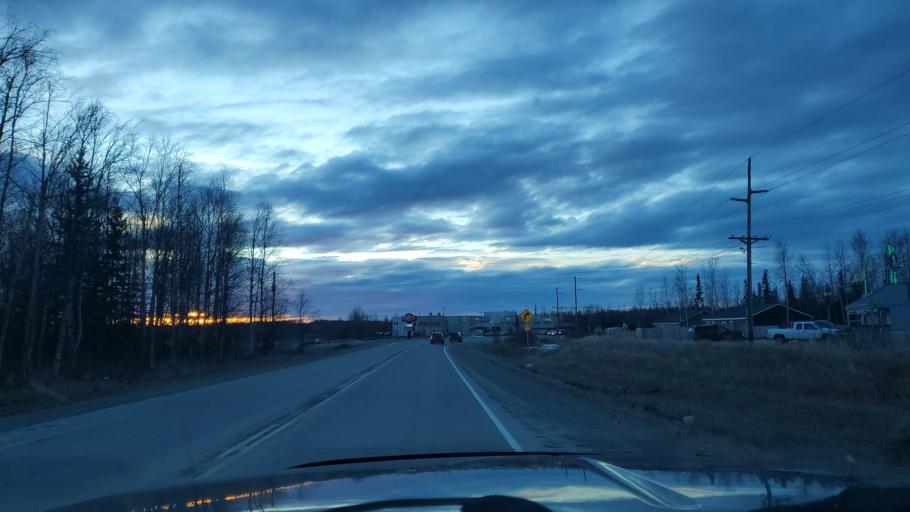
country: US
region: Alaska
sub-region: Matanuska-Susitna Borough
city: Wasilla
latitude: 61.5899
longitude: -149.4010
